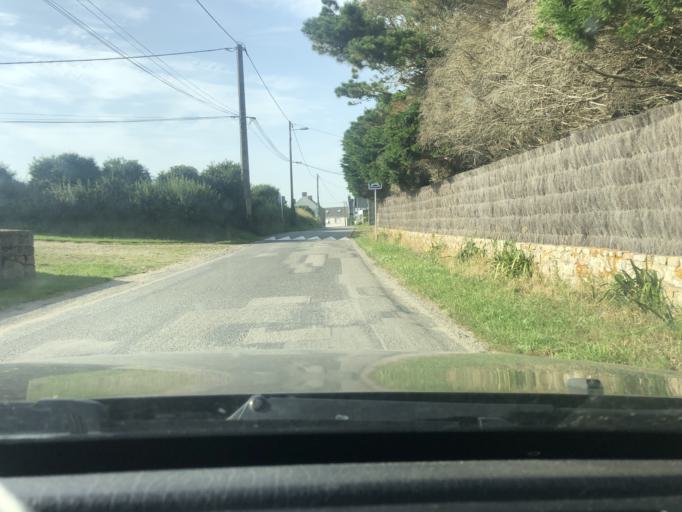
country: FR
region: Brittany
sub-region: Departement du Morbihan
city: Erdeven
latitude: 47.6254
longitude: -3.1805
